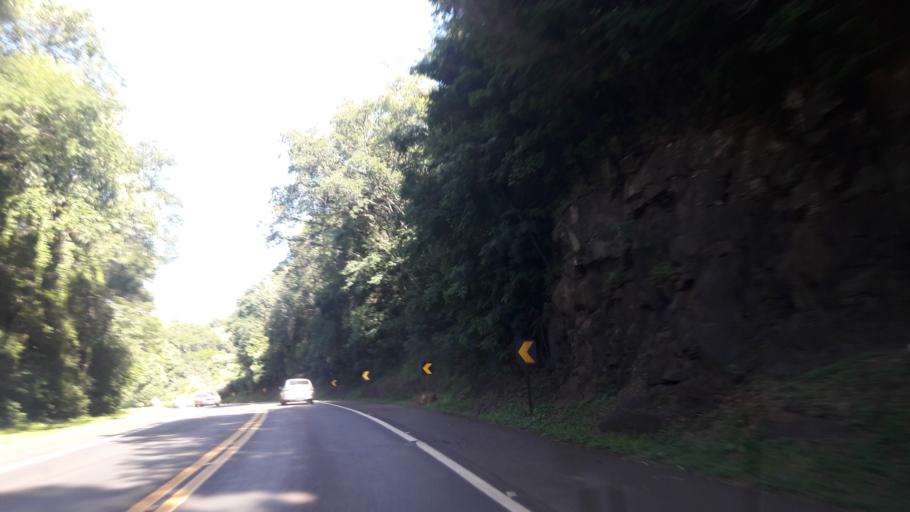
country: BR
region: Parana
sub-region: Laranjeiras Do Sul
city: Laranjeiras do Sul
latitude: -25.4202
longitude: -52.0645
